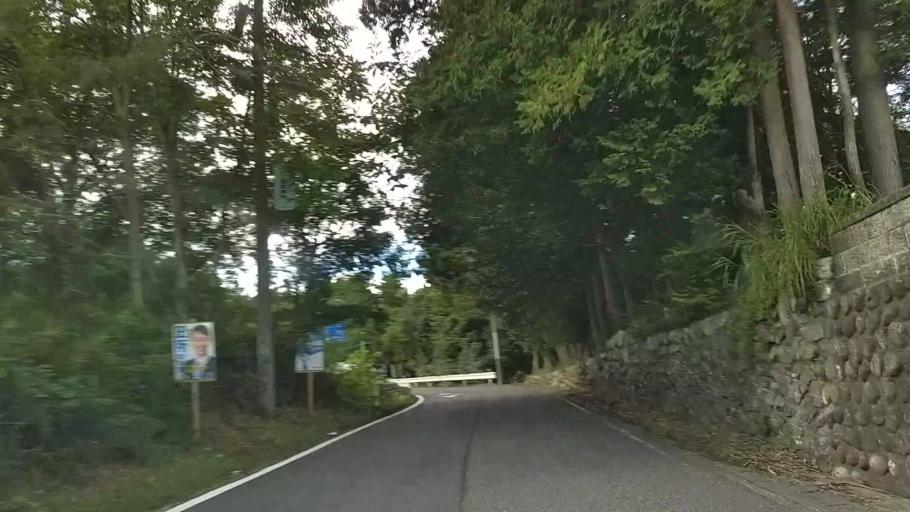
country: JP
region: Yamanashi
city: Uenohara
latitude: 35.5917
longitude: 139.1500
